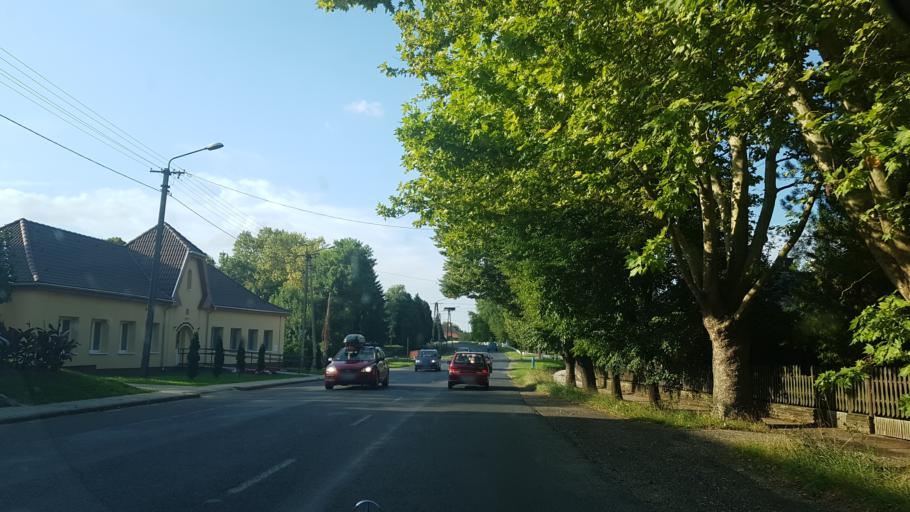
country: HU
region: Somogy
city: Nagyatad
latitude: 46.2855
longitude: 17.3609
